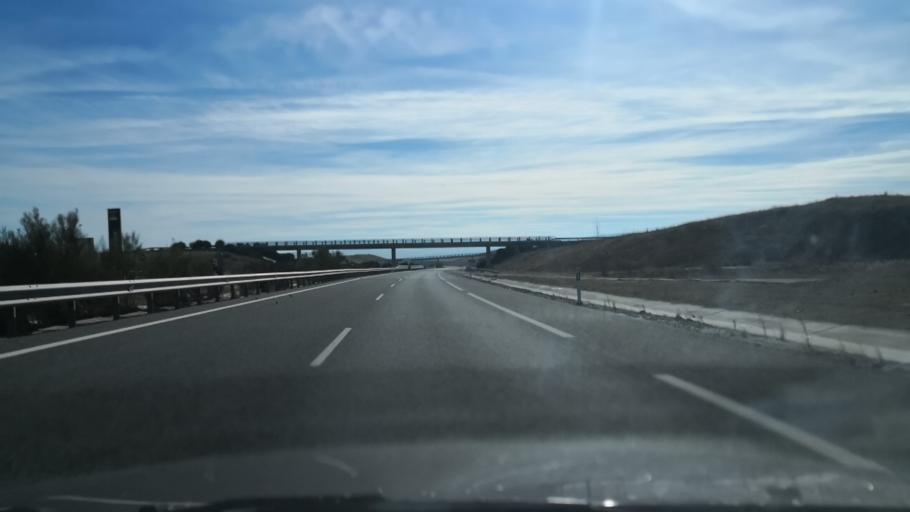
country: ES
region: Castille and Leon
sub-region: Provincia de Avila
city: Munogrande
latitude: 40.8284
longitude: -4.9370
